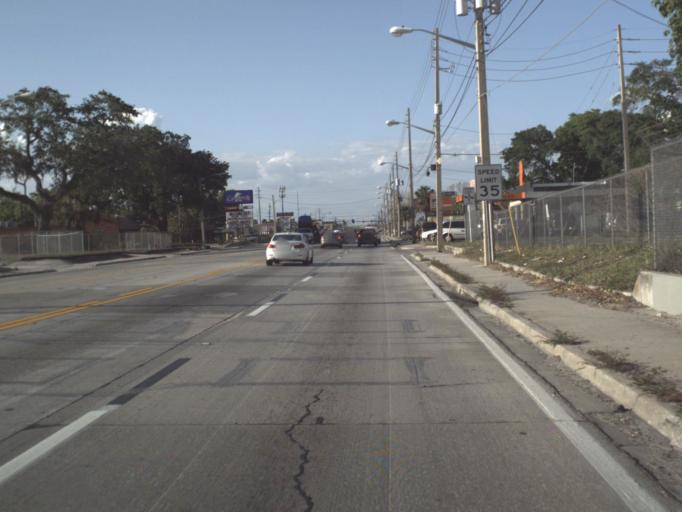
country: US
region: Florida
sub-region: Orange County
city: Orlando
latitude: 28.5273
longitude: -81.3970
